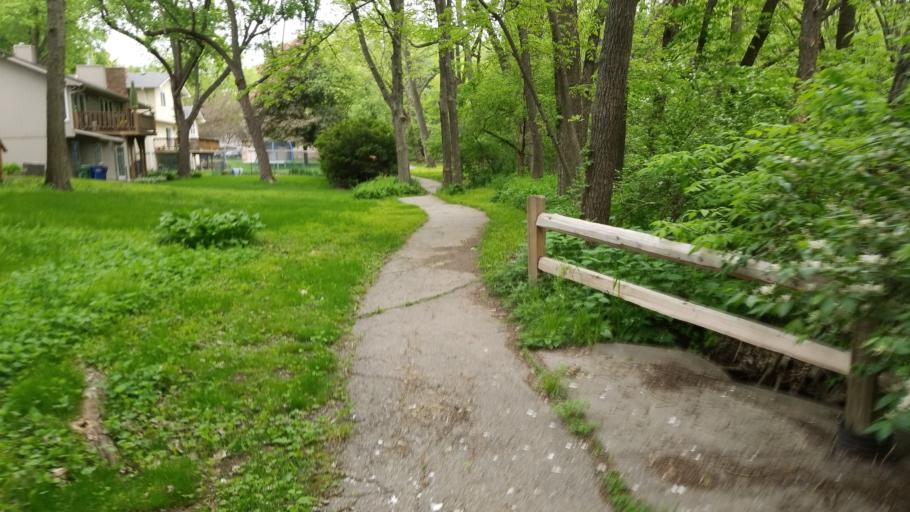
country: US
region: Nebraska
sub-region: Sarpy County
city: Offutt Air Force Base
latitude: 41.1343
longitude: -95.9726
